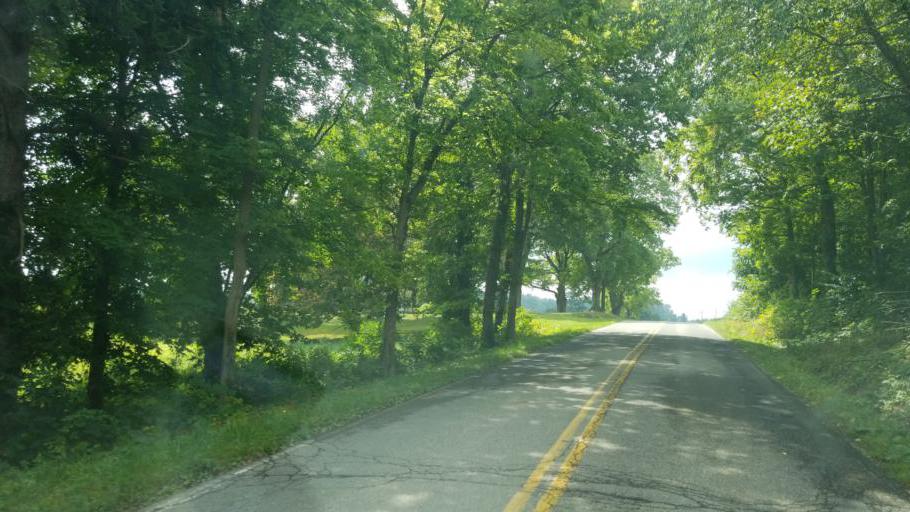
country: US
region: Ohio
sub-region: Licking County
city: Utica
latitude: 40.2190
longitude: -82.4584
